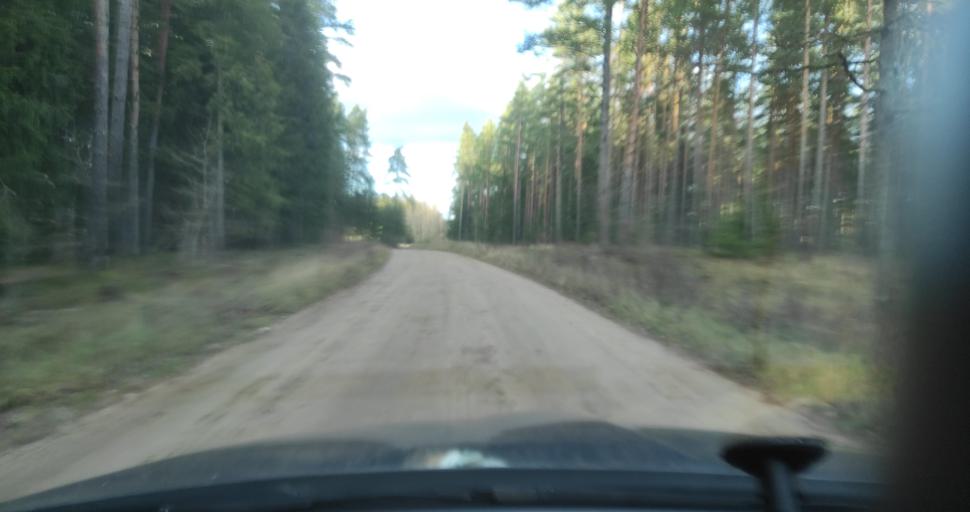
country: LV
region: Kuldigas Rajons
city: Kuldiga
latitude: 57.2843
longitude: 22.0392
